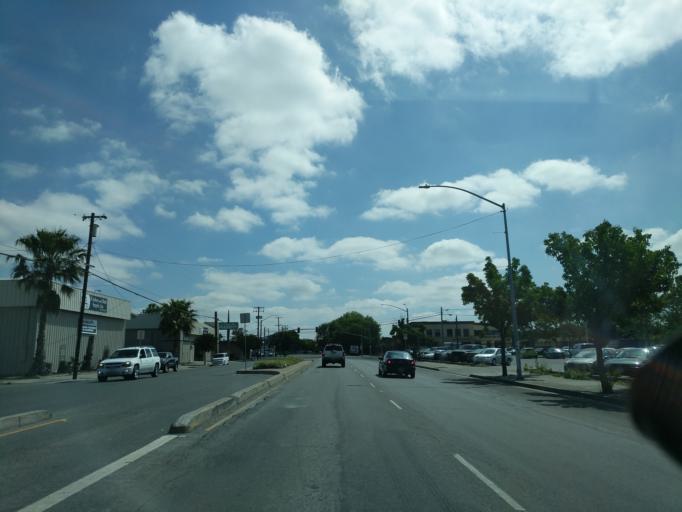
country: US
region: California
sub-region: San Joaquin County
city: Stockton
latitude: 37.9379
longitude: -121.2916
